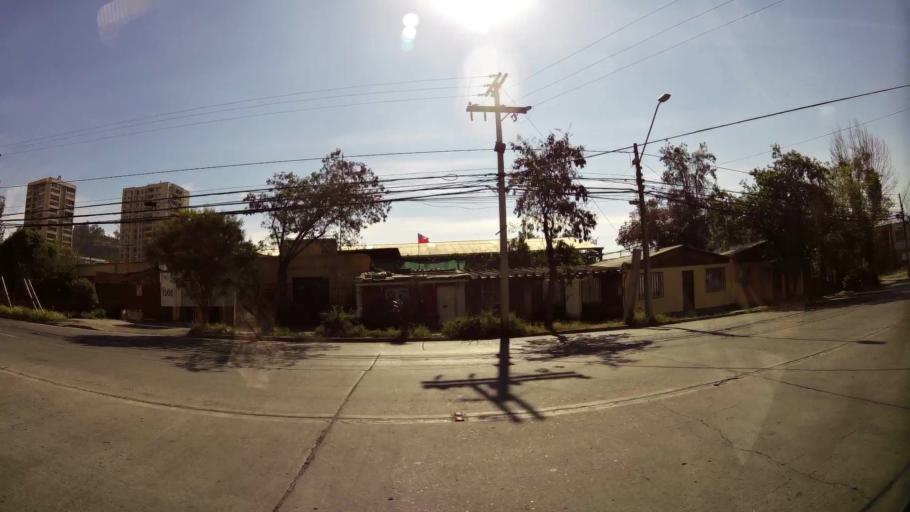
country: CL
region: Santiago Metropolitan
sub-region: Provincia de Santiago
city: Santiago
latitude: -33.4171
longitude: -70.6389
